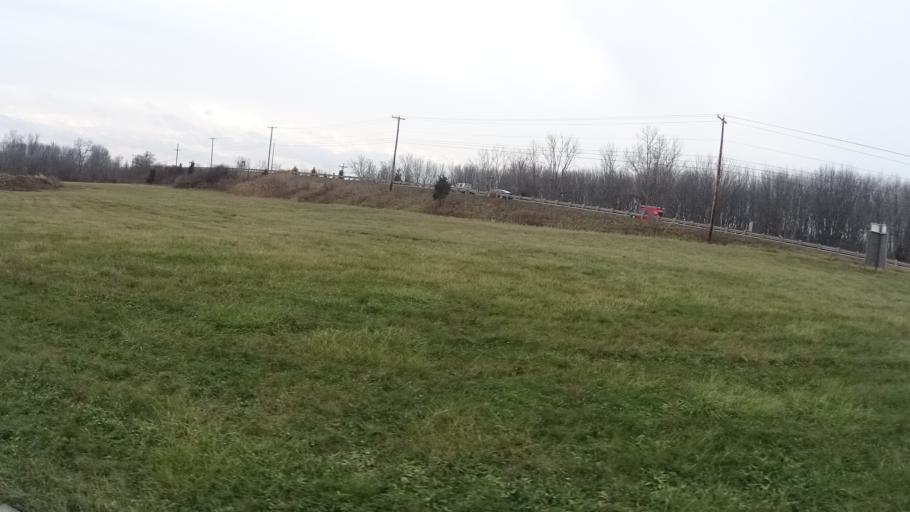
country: US
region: Ohio
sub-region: Lorain County
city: Amherst
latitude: 41.3953
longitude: -82.2091
